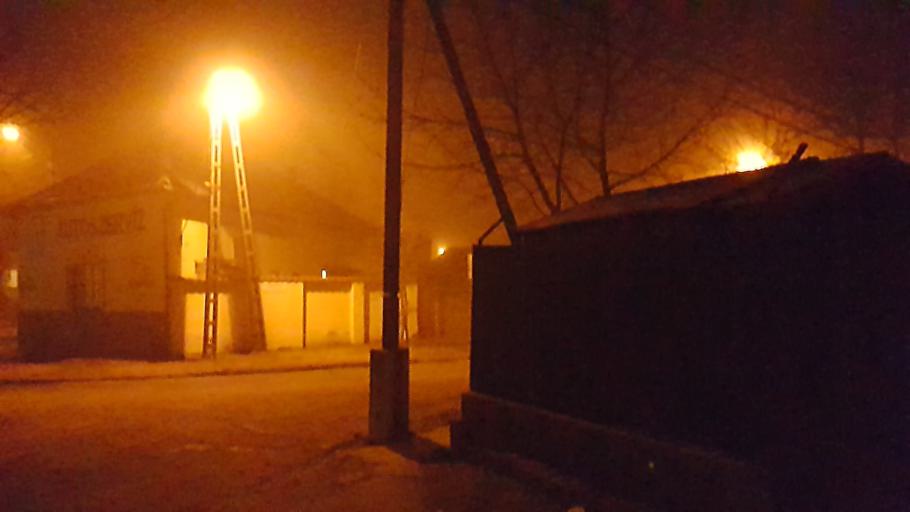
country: HU
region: Budapest
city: Budapest XIX. keruelet
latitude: 47.4382
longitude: 19.1289
